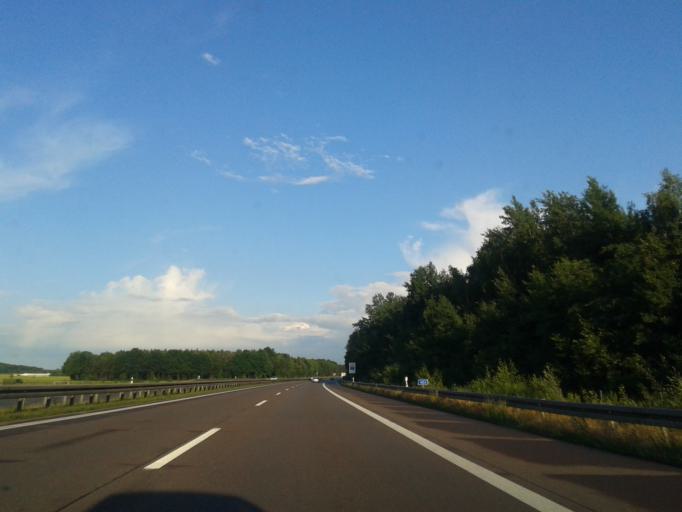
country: DE
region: Saxony
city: Naunhof
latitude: 51.3019
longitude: 12.6078
